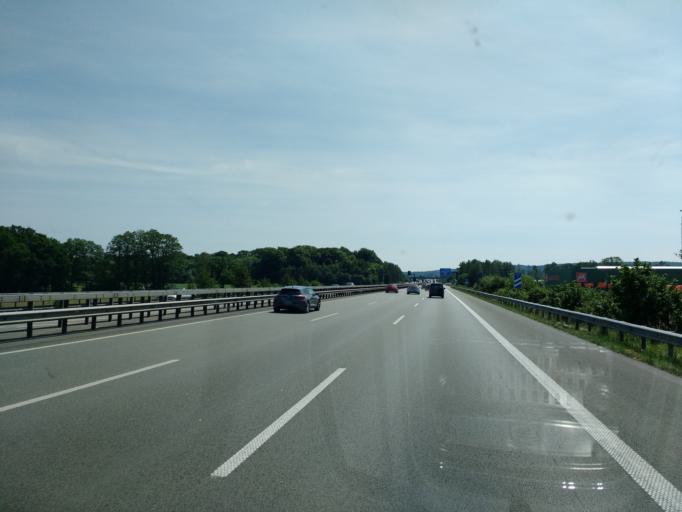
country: DE
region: Lower Saxony
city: Wallenhorst
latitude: 52.4016
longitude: 8.0349
